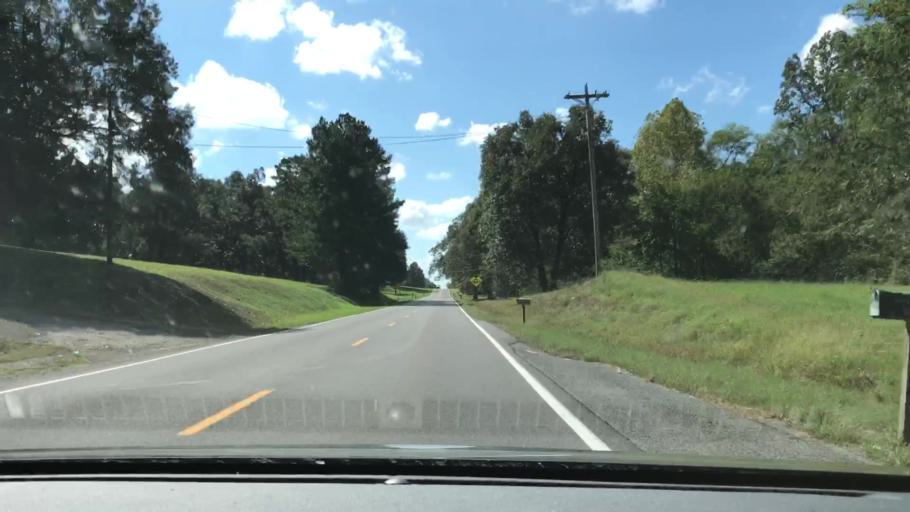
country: US
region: Kentucky
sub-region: McCracken County
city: Reidland
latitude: 36.9093
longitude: -88.5230
